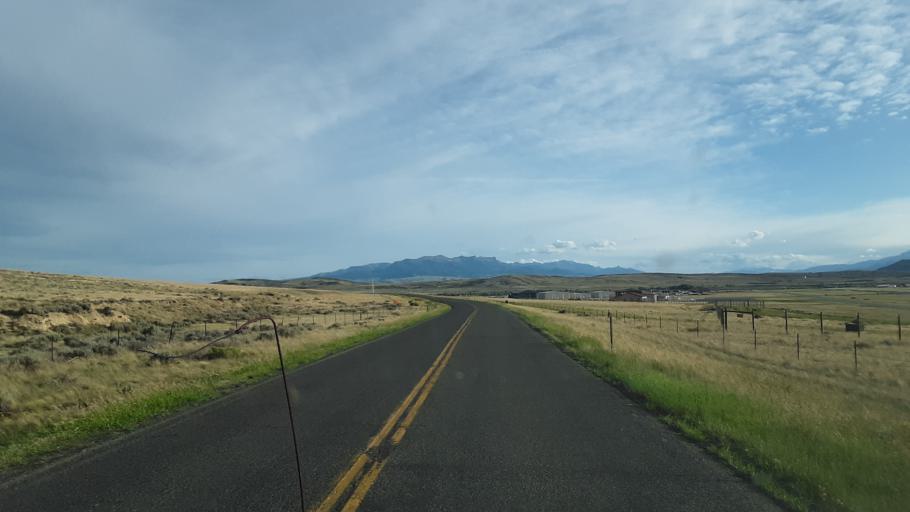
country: US
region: Wyoming
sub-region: Park County
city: Cody
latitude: 44.5227
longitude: -109.0147
